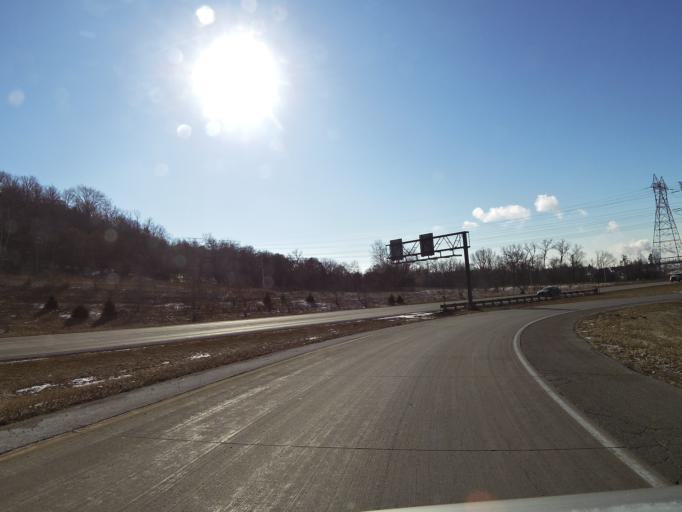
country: US
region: Minnesota
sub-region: Washington County
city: Newport
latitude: 44.8857
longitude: -93.0023
